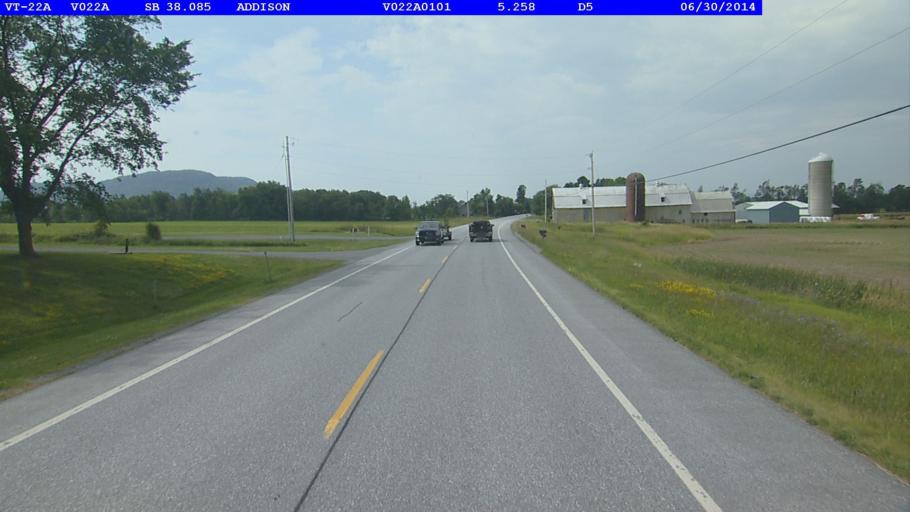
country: US
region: Vermont
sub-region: Addison County
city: Vergennes
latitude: 44.1045
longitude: -73.2957
